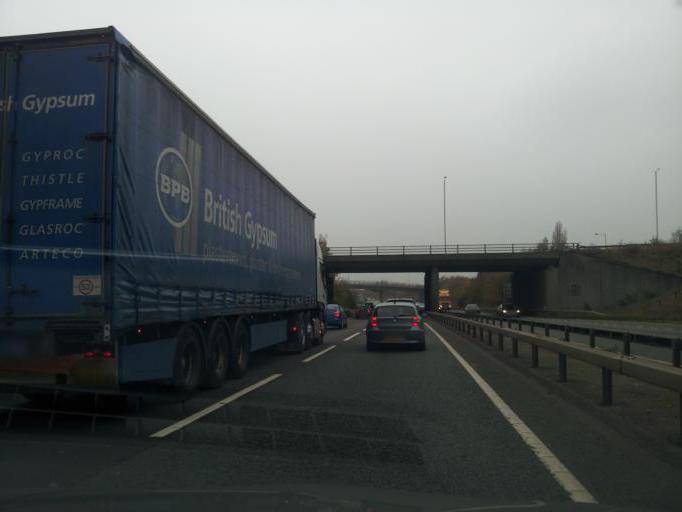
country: GB
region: England
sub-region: Leicestershire
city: Glenfield
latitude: 52.6618
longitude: -1.2048
